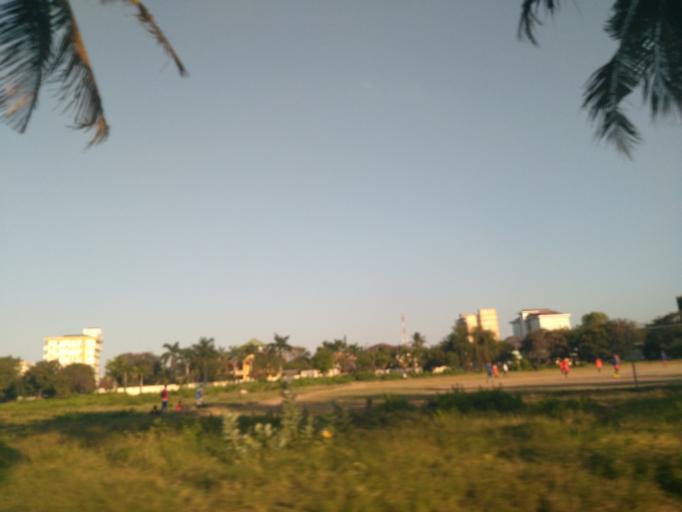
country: TZ
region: Dar es Salaam
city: Magomeni
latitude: -6.7599
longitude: 39.2526
